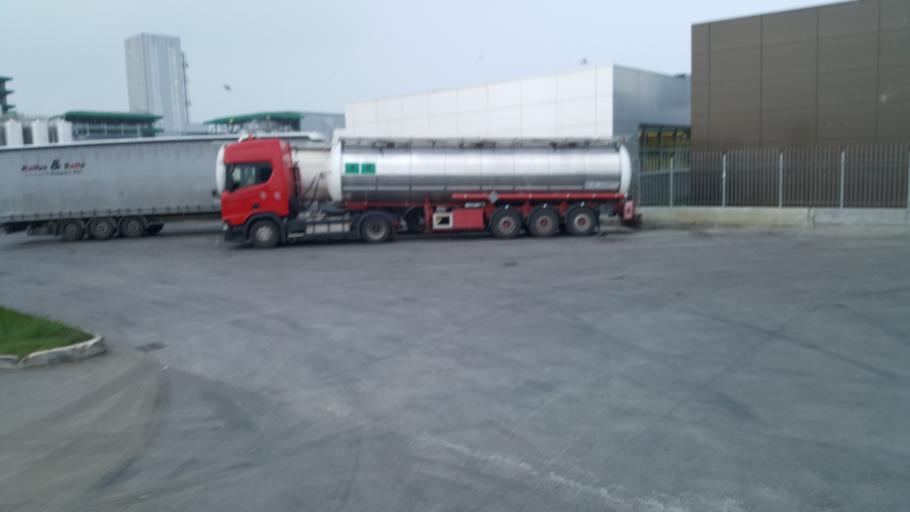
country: IT
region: Emilia-Romagna
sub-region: Provincia di Ravenna
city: Lavezzola
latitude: 44.5331
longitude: 11.8600
